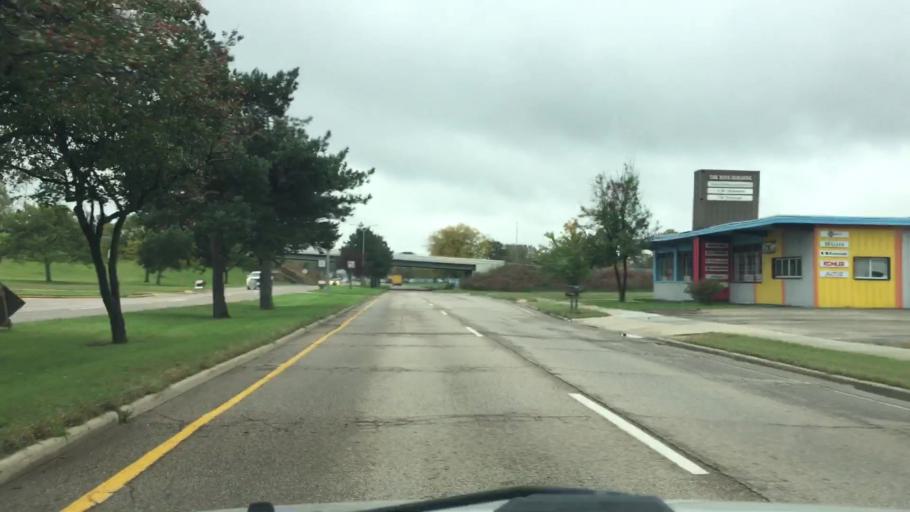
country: US
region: Wisconsin
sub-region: Rock County
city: Janesville
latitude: 42.6955
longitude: -89.0299
